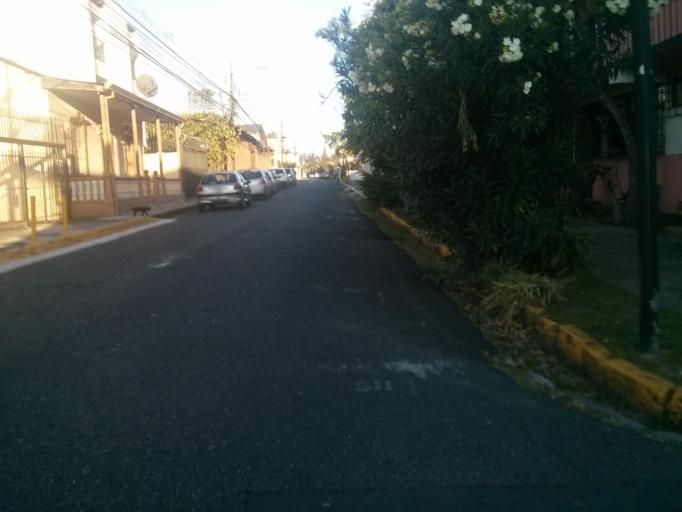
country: CR
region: San Jose
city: San Jose
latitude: 9.9330
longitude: -84.0669
